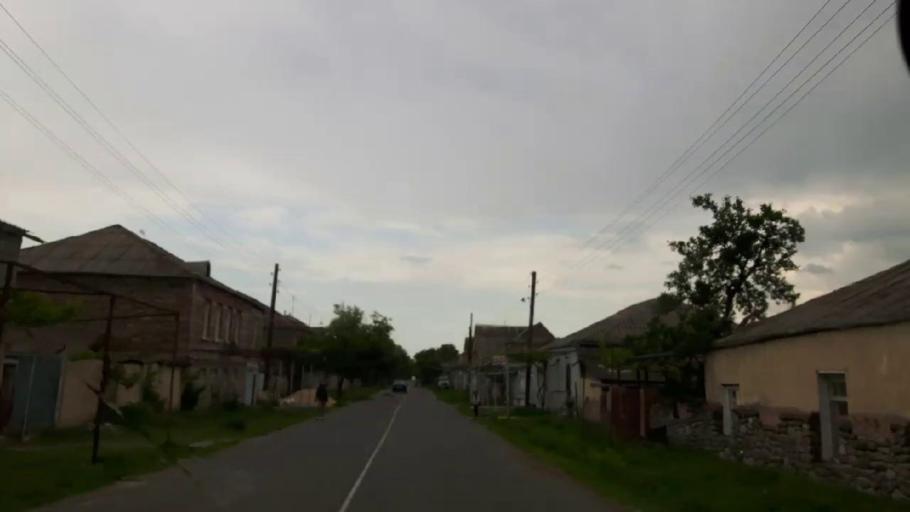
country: GE
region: Shida Kartli
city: Gori
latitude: 41.9607
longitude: 44.2044
